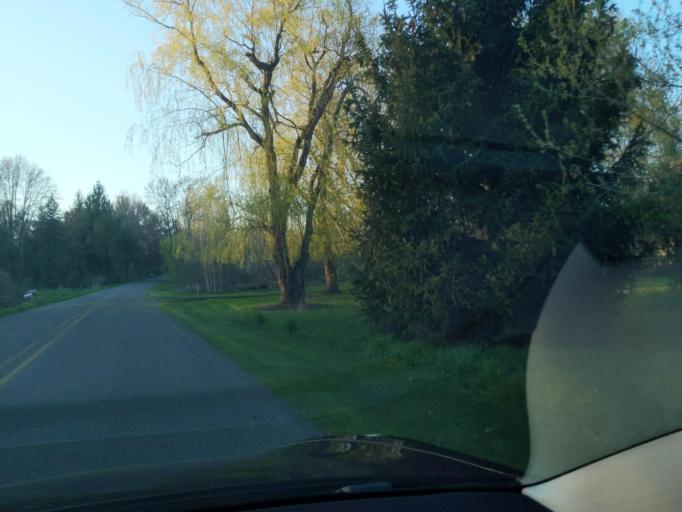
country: US
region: Michigan
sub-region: Ingham County
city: Stockbridge
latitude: 42.4947
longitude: -84.2945
